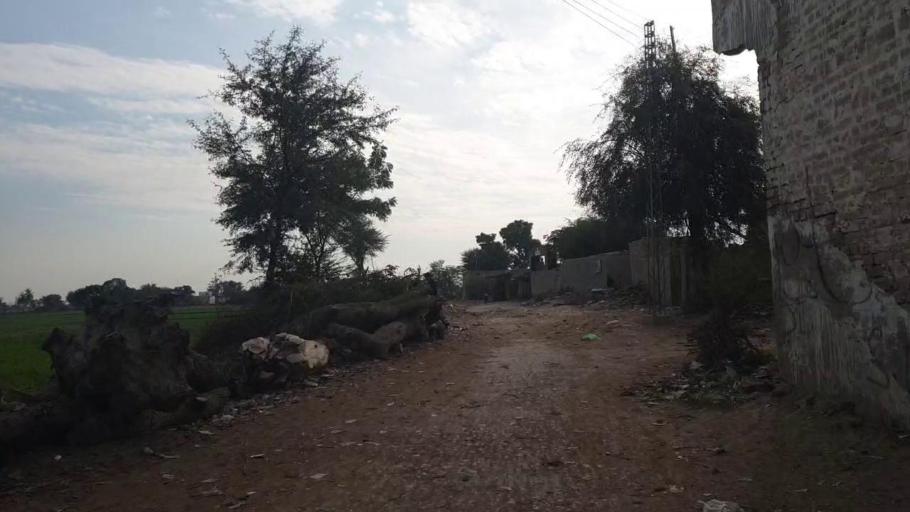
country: PK
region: Sindh
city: Shahpur Chakar
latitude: 26.0561
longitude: 68.5798
